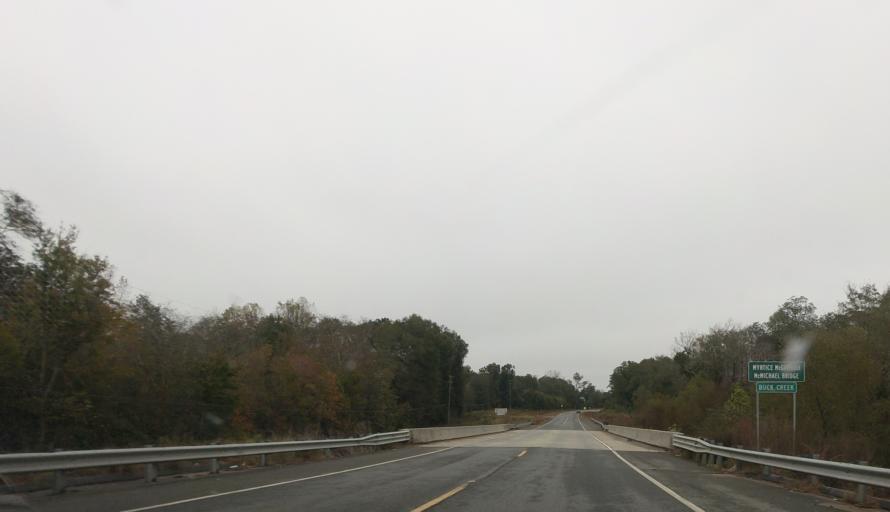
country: US
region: Georgia
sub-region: Marion County
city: Buena Vista
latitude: 32.3778
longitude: -84.4472
